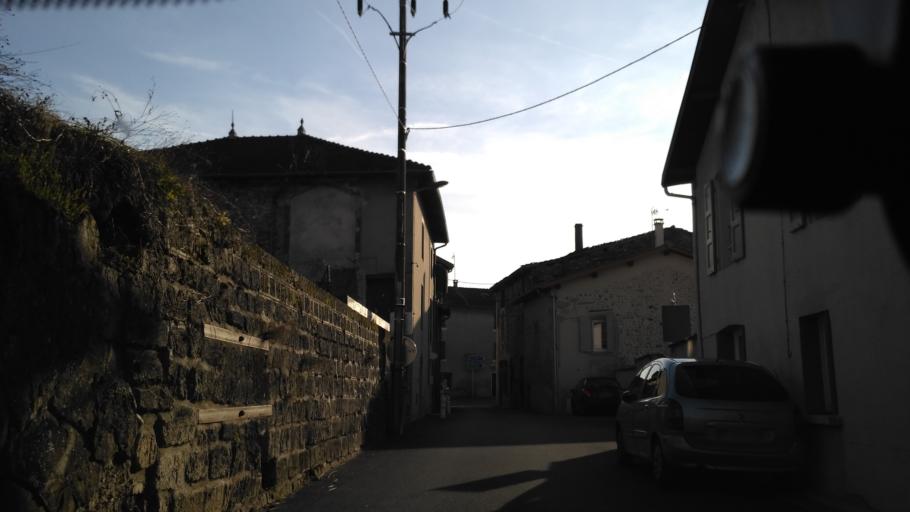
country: FR
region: Rhone-Alpes
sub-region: Departement de la Drome
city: Saint-Paul-les-Romans
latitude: 45.0708
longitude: 5.1332
